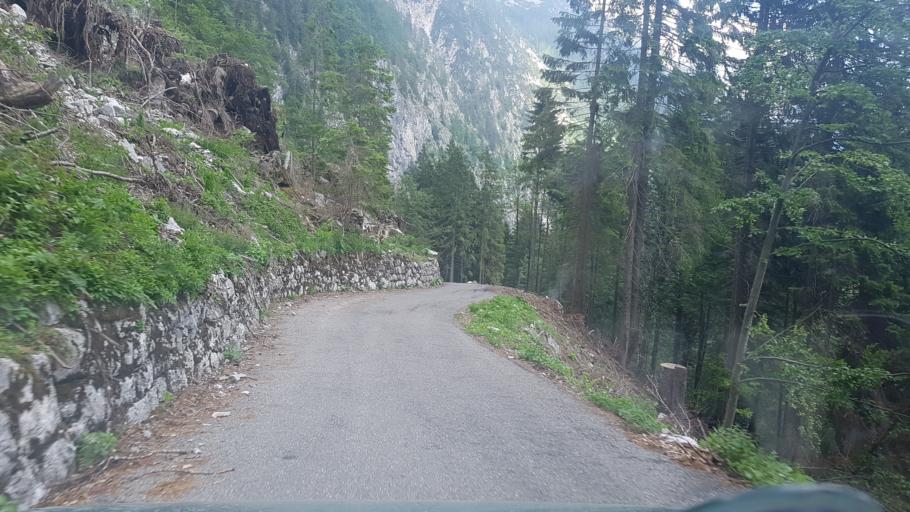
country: IT
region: Friuli Venezia Giulia
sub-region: Provincia di Udine
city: Paularo
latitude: 46.5518
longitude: 13.1939
